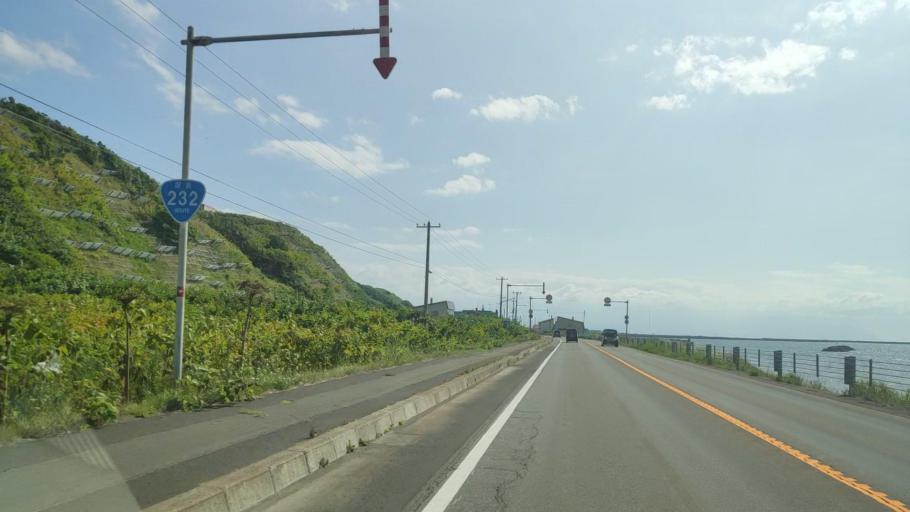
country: JP
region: Hokkaido
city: Rumoi
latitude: 43.9866
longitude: 141.6492
